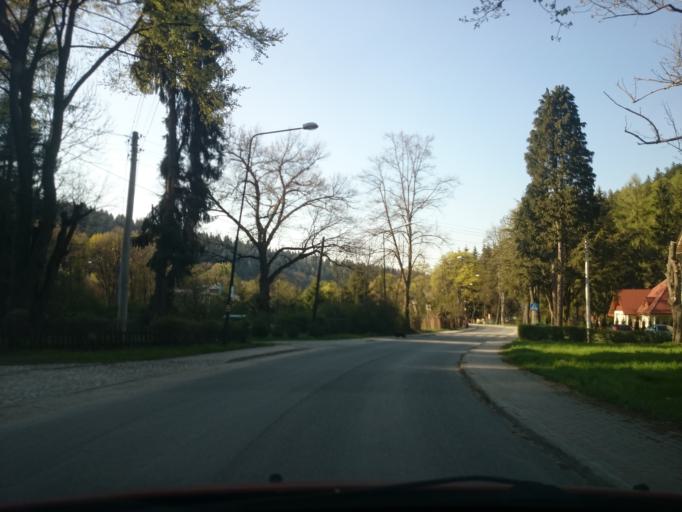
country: PL
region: Lower Silesian Voivodeship
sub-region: Powiat klodzki
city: Duszniki-Zdroj
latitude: 50.3870
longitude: 16.3840
